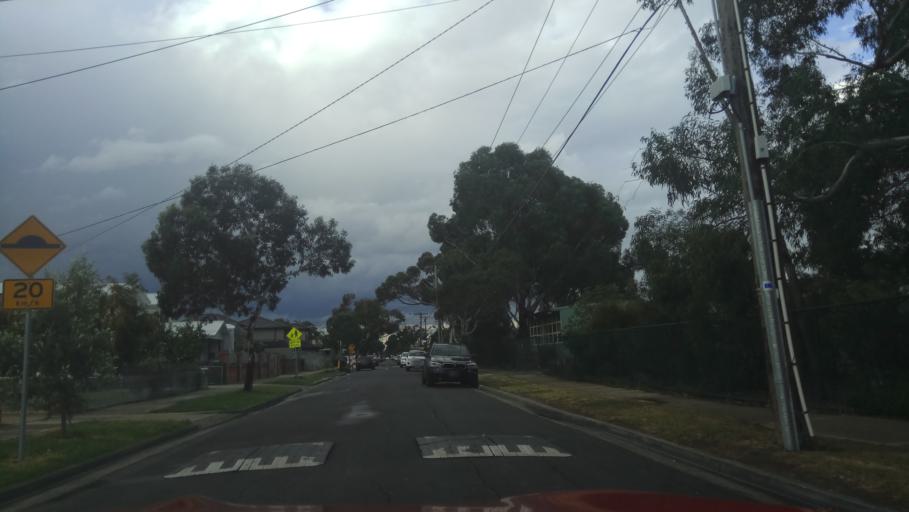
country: AU
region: Victoria
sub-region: Hobsons Bay
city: Altona North
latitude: -37.8380
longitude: 144.8482
